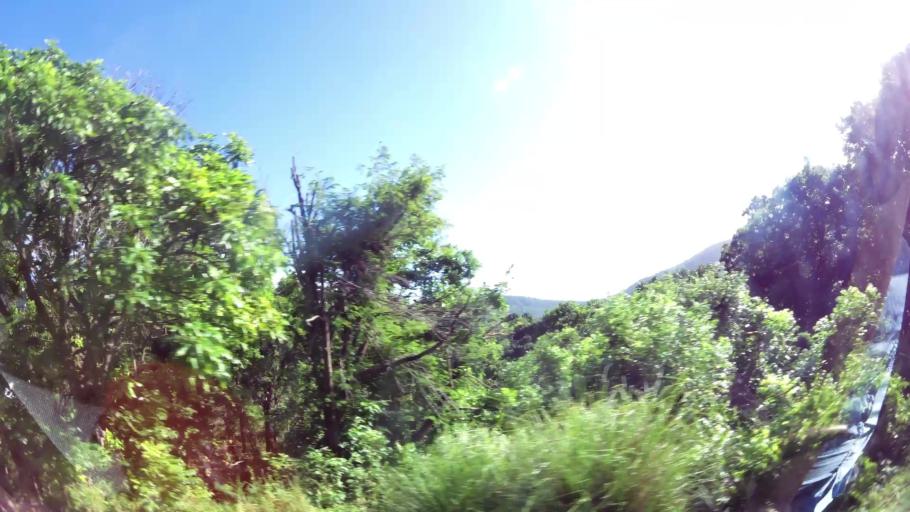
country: MS
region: Saint Peter
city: Saint Peters
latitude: 16.7495
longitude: -62.2182
